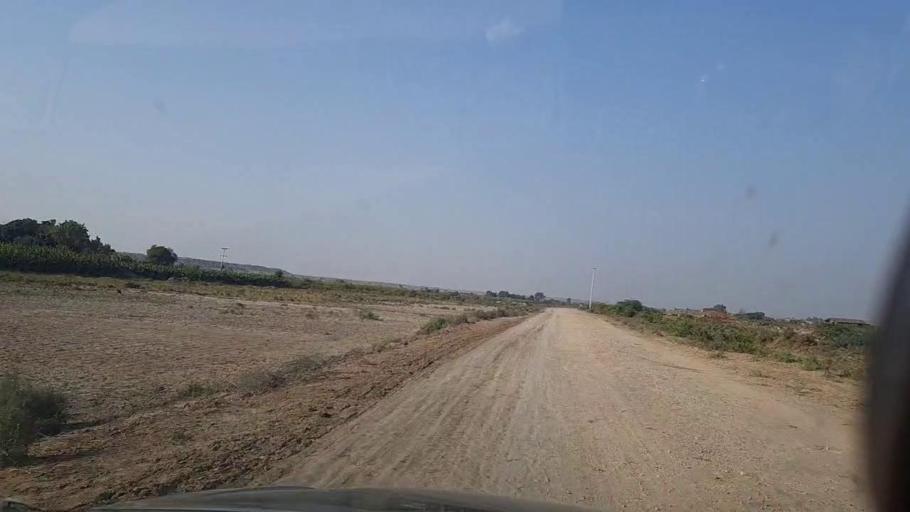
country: PK
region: Sindh
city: Thatta
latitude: 24.5971
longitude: 67.8745
